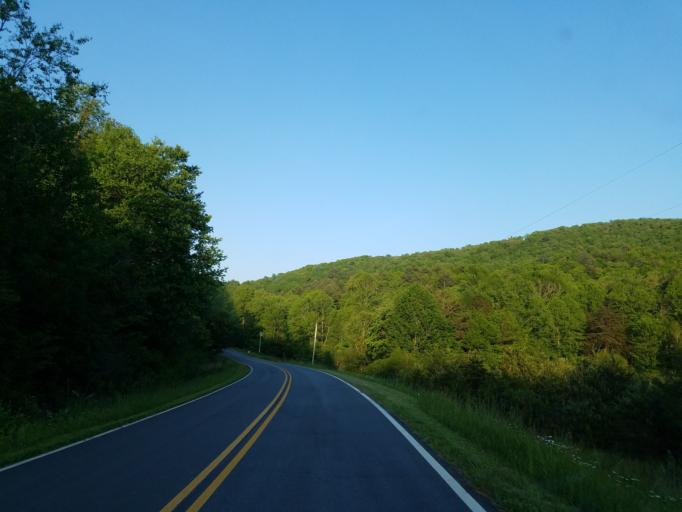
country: US
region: Georgia
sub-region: Union County
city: Blairsville
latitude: 34.7441
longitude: -84.0464
